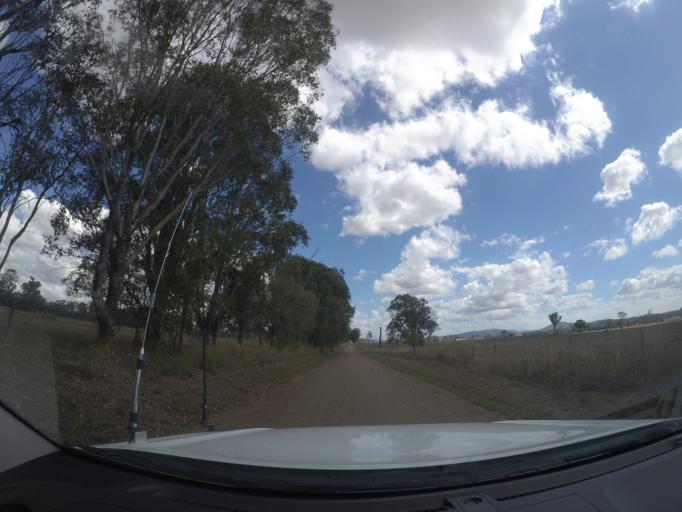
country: AU
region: Queensland
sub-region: Logan
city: Cedar Vale
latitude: -27.8896
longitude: 152.9598
